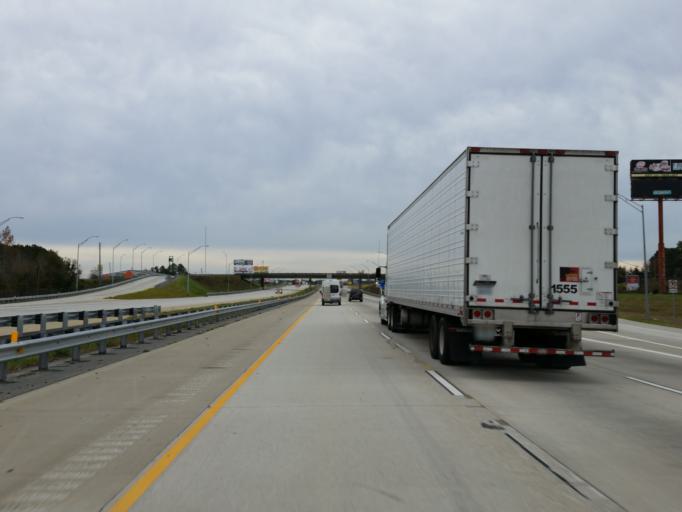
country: US
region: Georgia
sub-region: Dooly County
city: Unadilla
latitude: 32.2632
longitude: -83.7505
